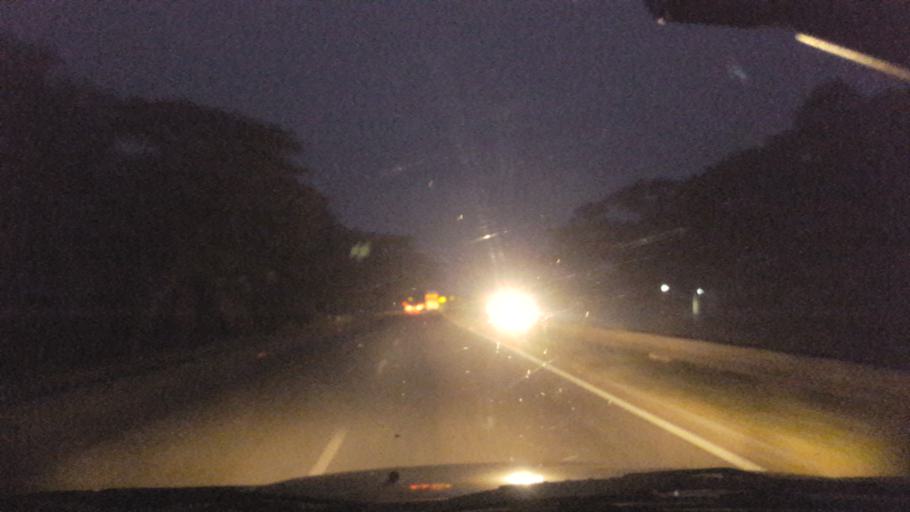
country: IN
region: Andhra Pradesh
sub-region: East Godavari
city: Peddapuram
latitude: 17.1374
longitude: 81.9636
